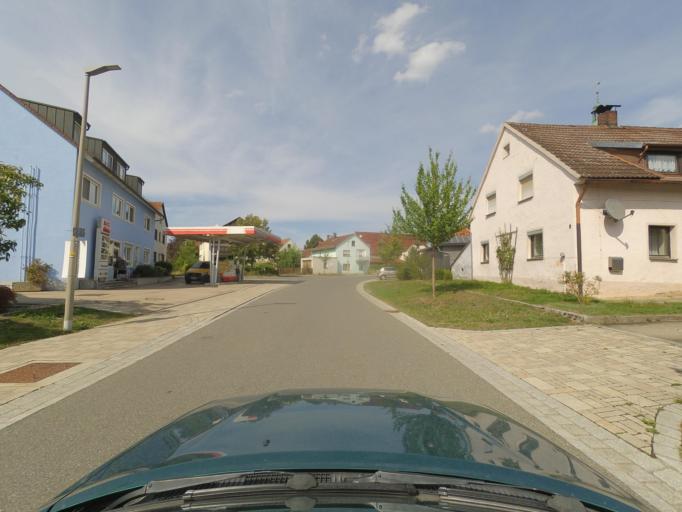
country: DE
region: Bavaria
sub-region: Upper Palatinate
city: Freystadt
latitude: 49.1664
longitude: 11.3570
